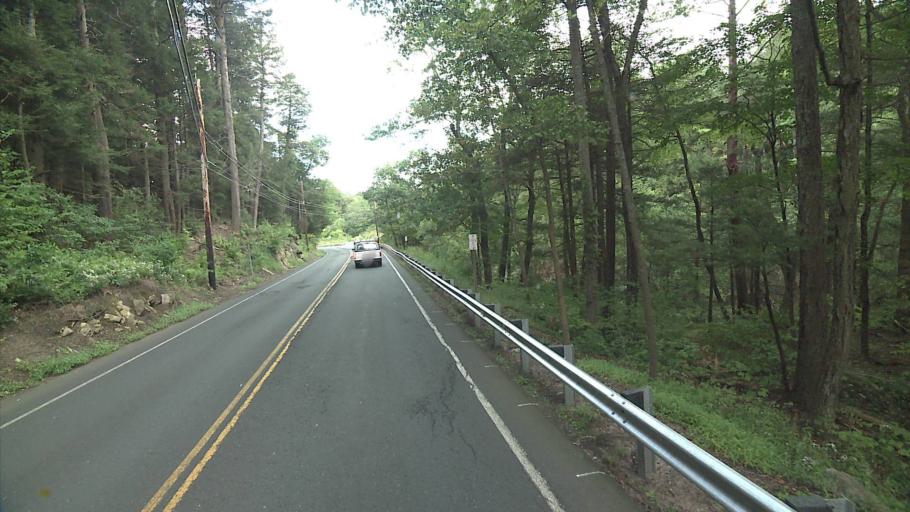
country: US
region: Connecticut
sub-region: Hartford County
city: North Granby
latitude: 42.0006
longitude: -72.8333
